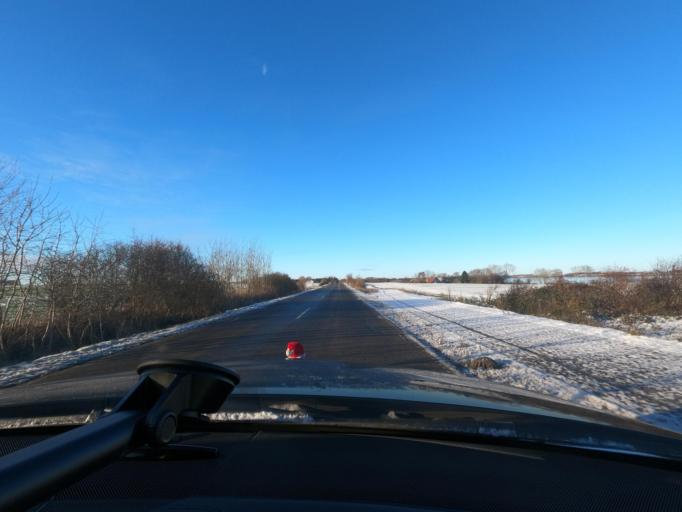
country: DK
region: South Denmark
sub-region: Sonderborg Kommune
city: Horuphav
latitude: 54.8649
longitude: 9.9620
